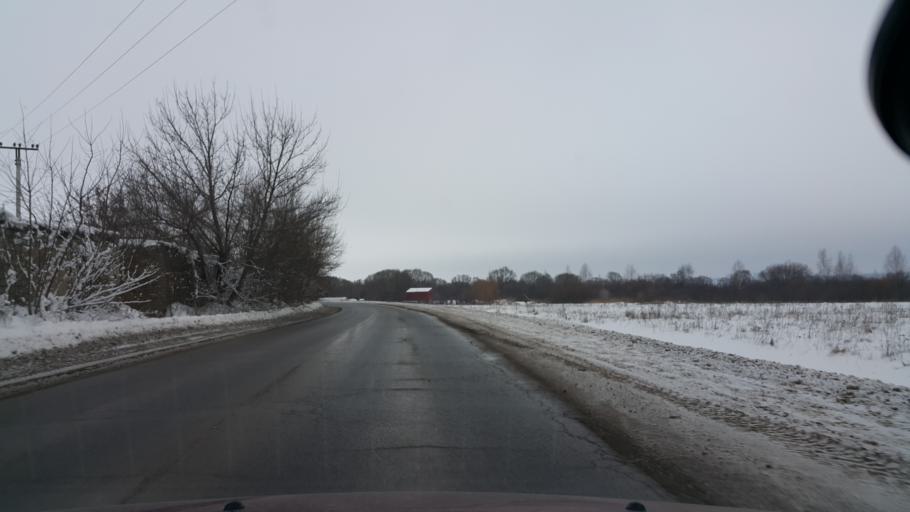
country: RU
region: Tambov
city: Pokrovo-Prigorodnoye
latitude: 52.6600
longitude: 41.4364
